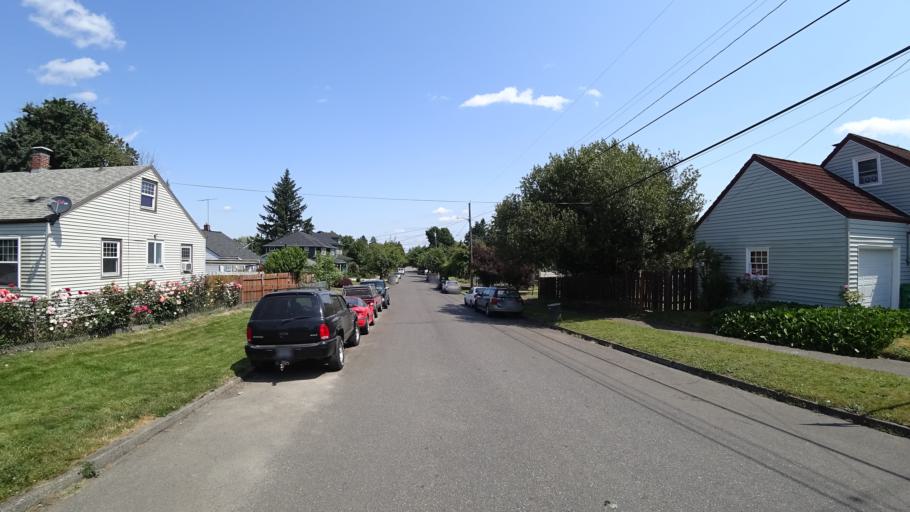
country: US
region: Oregon
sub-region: Washington County
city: West Haven
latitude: 45.5950
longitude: -122.7412
